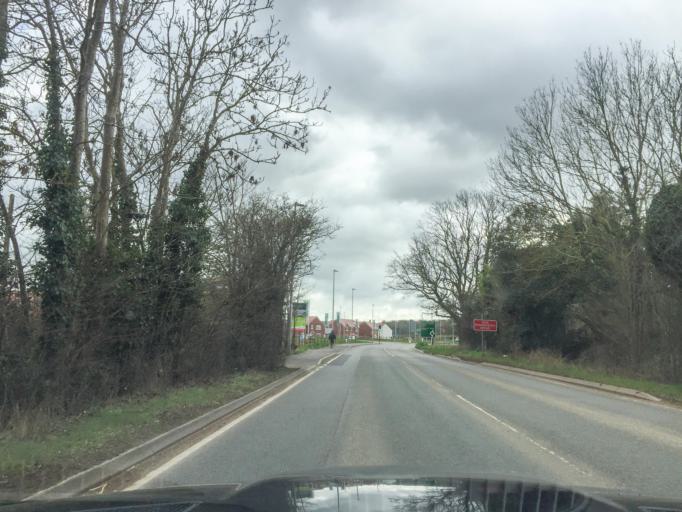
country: GB
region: England
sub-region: Warwickshire
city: Wellesbourne Mountford
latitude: 52.1859
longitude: -1.5979
